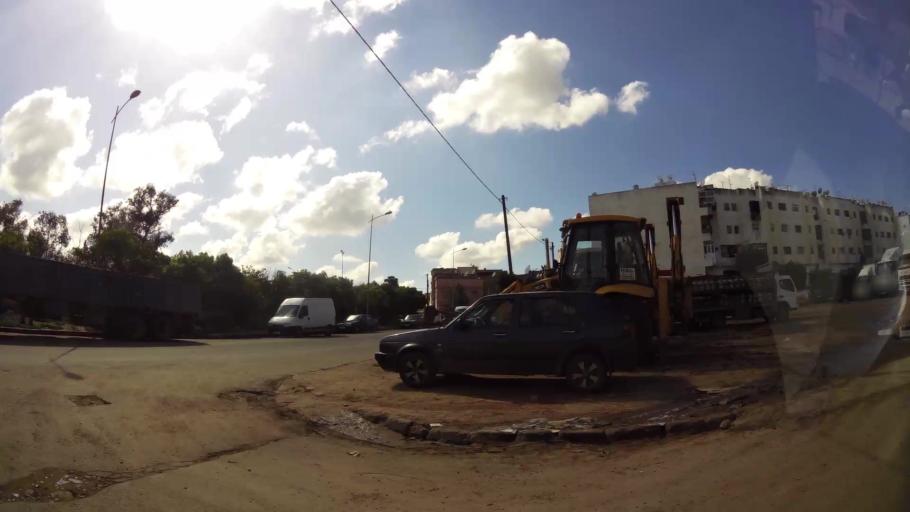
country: MA
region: Grand Casablanca
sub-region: Mediouna
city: Mediouna
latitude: 33.4559
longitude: -7.5170
